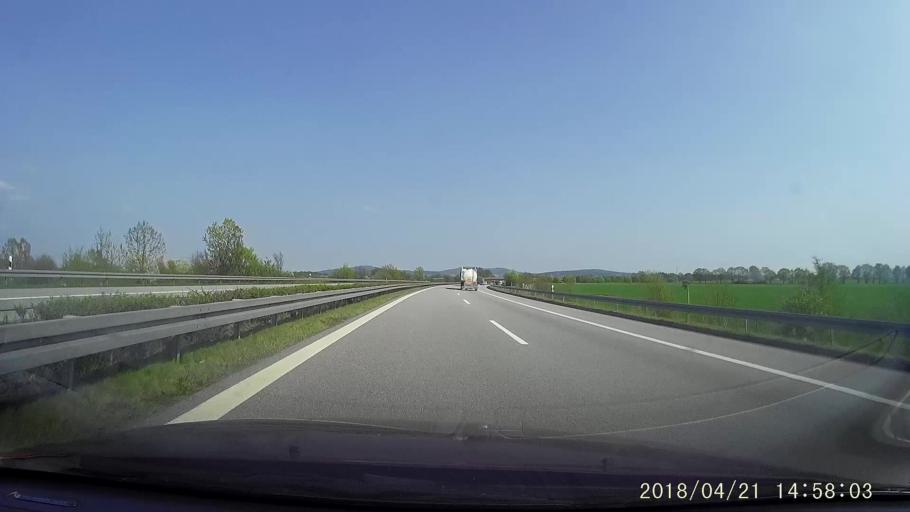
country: DE
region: Saxony
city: Weissenberg
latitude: 51.2129
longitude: 14.7235
